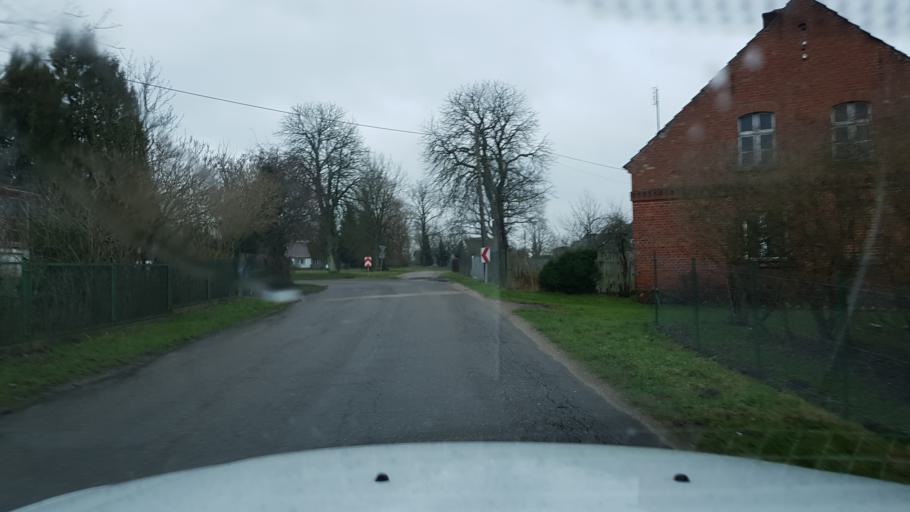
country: PL
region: West Pomeranian Voivodeship
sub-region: Powiat gryficki
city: Brojce
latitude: 53.9923
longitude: 15.3141
